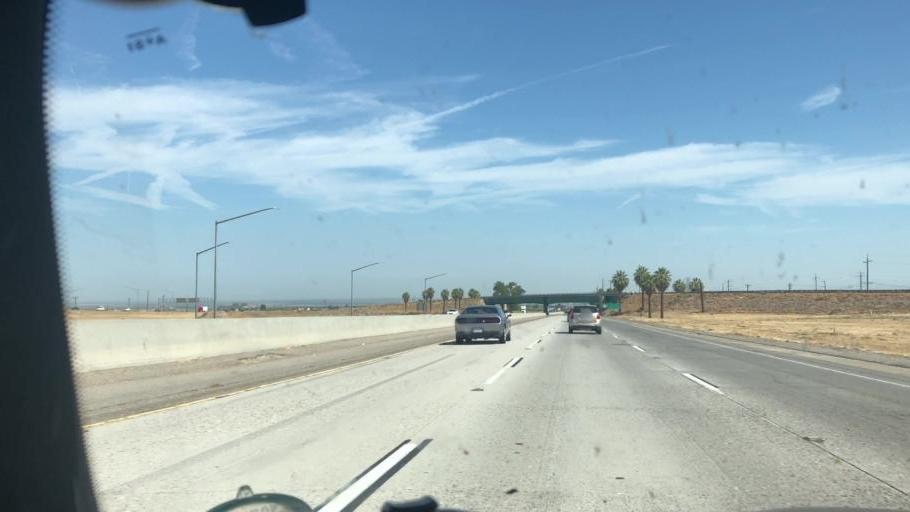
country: US
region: California
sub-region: Kern County
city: Frazier Park
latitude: 35.0154
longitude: -118.9544
